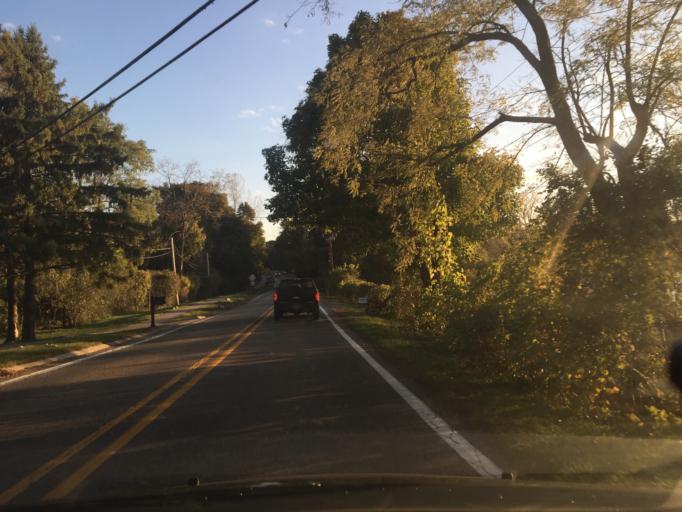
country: US
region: Michigan
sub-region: Oakland County
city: Bloomfield Hills
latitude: 42.5853
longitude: -83.2864
